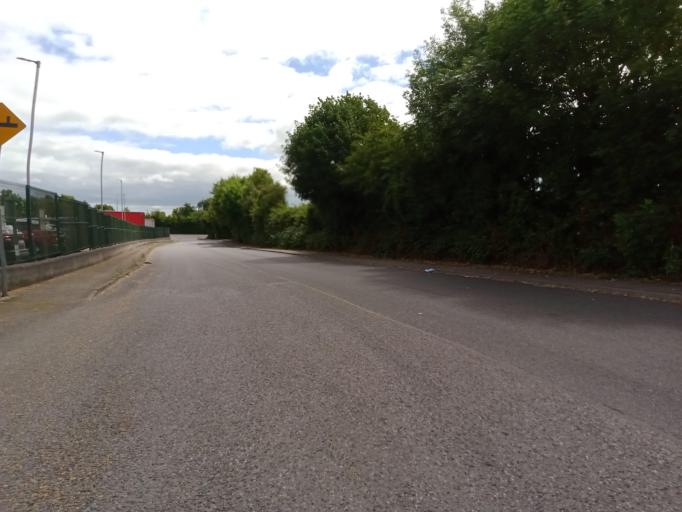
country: IE
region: Leinster
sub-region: Kilkenny
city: Callan
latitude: 52.5554
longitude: -7.3805
